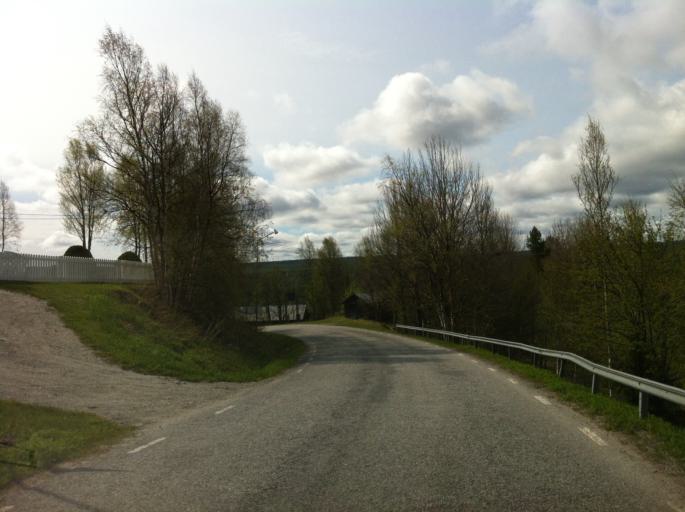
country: NO
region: Hedmark
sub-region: Engerdal
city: Engerdal
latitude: 62.4394
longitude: 12.6933
